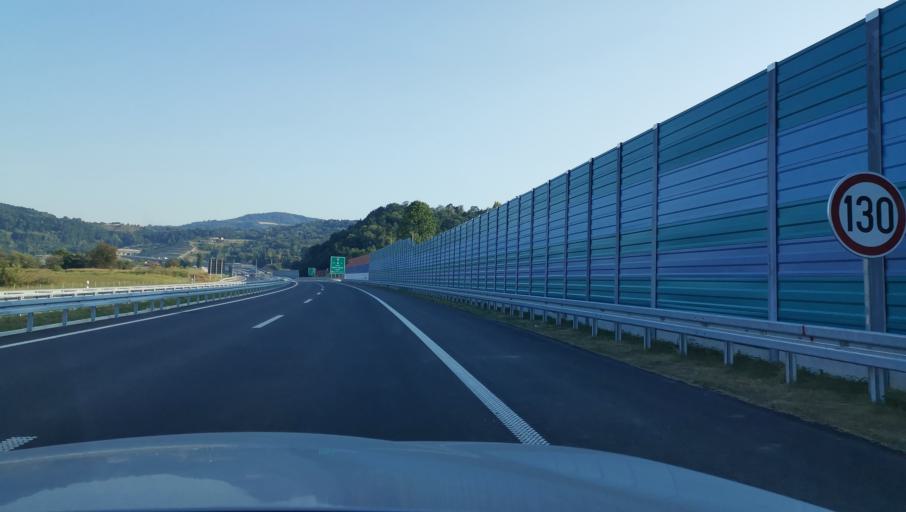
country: RS
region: Central Serbia
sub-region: Kolubarski Okrug
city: Ljig
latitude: 44.2287
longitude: 20.2535
